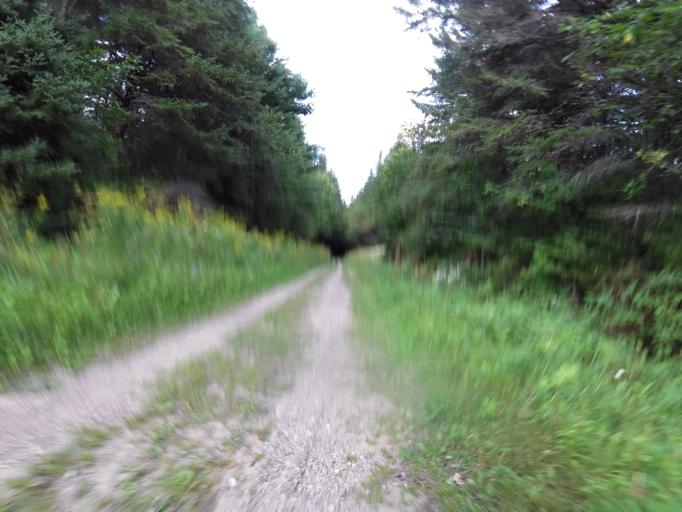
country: CA
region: Quebec
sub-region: Outaouais
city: Wakefield
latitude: 45.6319
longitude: -75.9450
